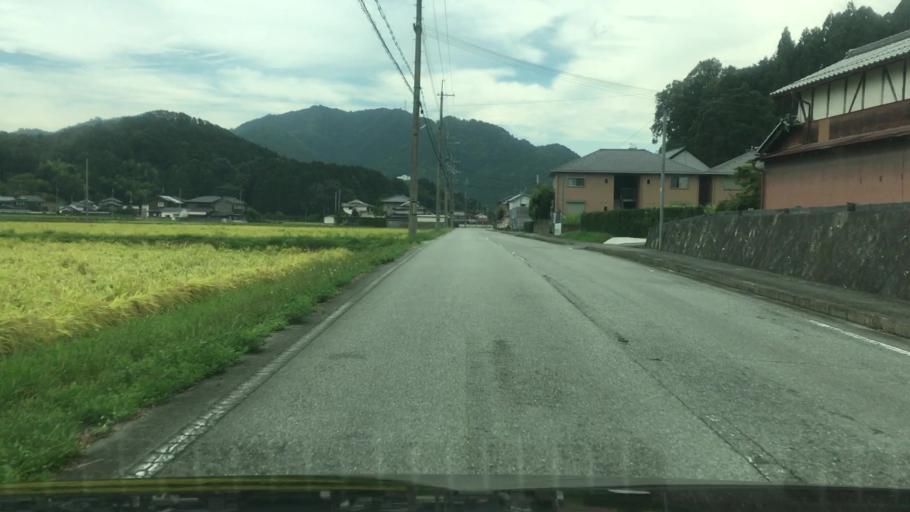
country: JP
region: Hyogo
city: Sasayama
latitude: 35.0717
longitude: 135.1839
